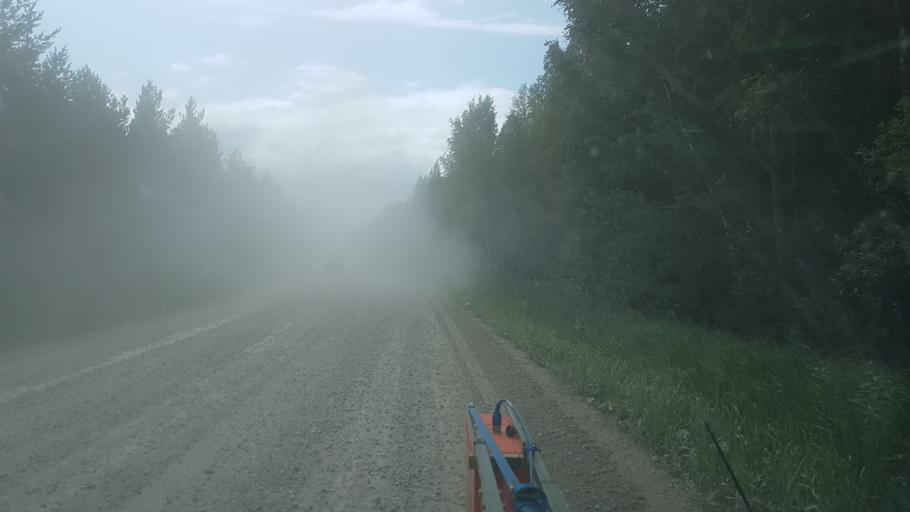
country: EE
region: Paernumaa
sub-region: Halinga vald
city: Parnu-Jaagupi
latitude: 58.5330
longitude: 24.4052
